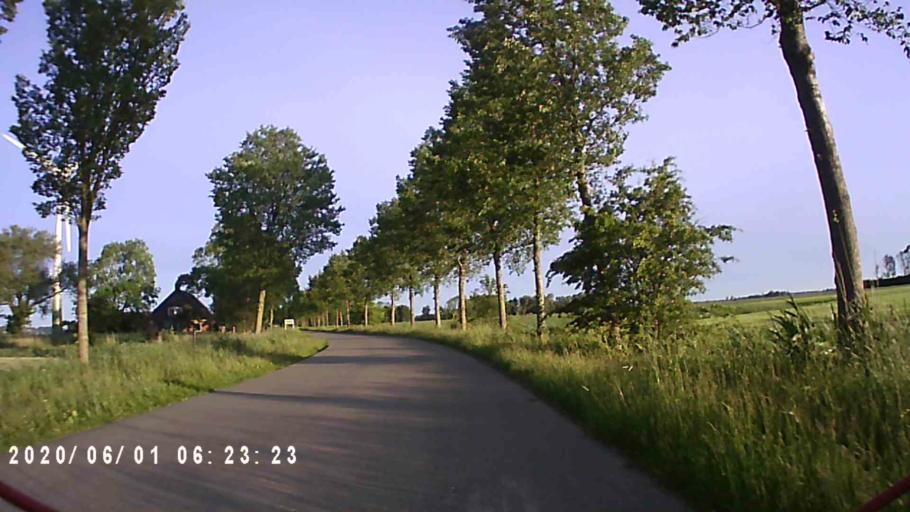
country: NL
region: Friesland
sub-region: Gemeente Kollumerland en Nieuwkruisland
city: Kollum
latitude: 53.2658
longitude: 6.2163
